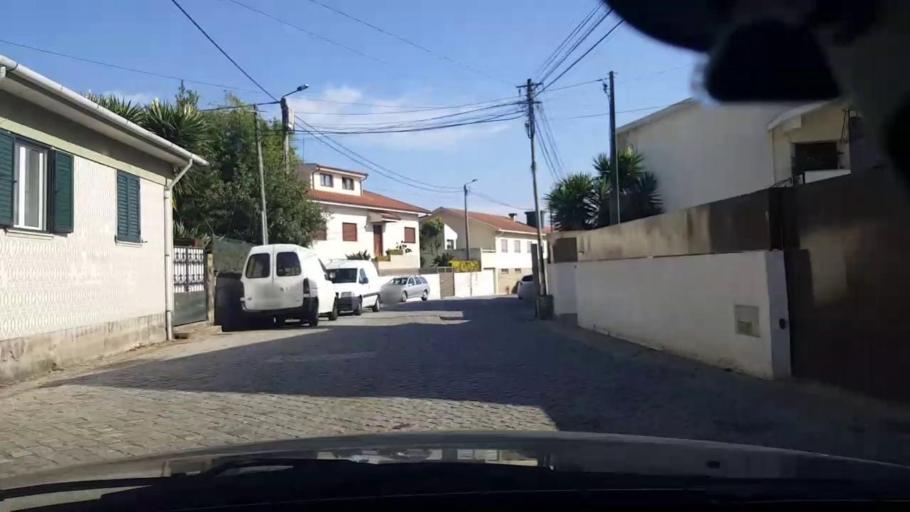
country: PT
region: Porto
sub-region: Maia
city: Gemunde
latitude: 41.2717
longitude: -8.6652
